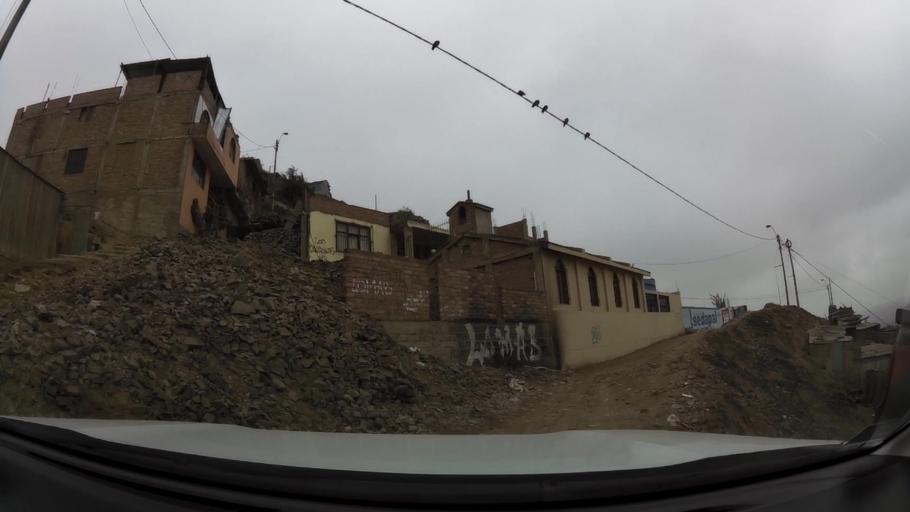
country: PE
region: Lima
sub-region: Lima
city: Surco
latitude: -12.1762
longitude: -76.9547
